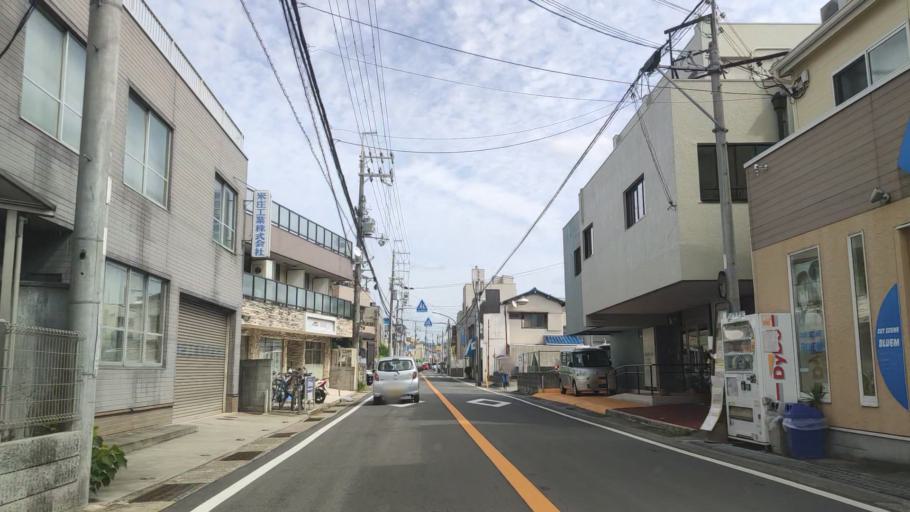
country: JP
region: Osaka
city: Mino
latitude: 34.8100
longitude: 135.4662
